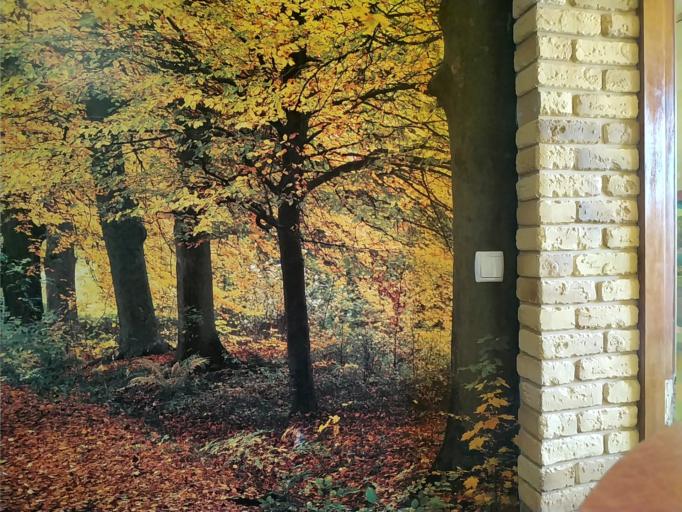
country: RU
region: Vologda
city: Nelazskoye
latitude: 59.4651
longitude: 37.6059
